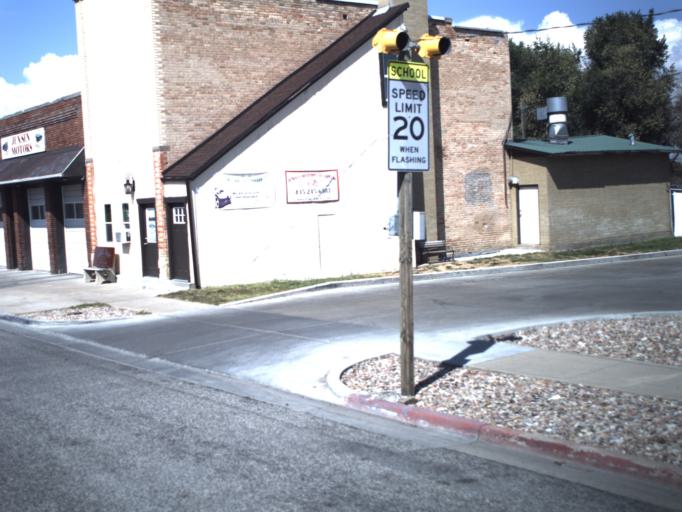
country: US
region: Utah
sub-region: Cache County
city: Hyrum
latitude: 41.6341
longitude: -111.8542
